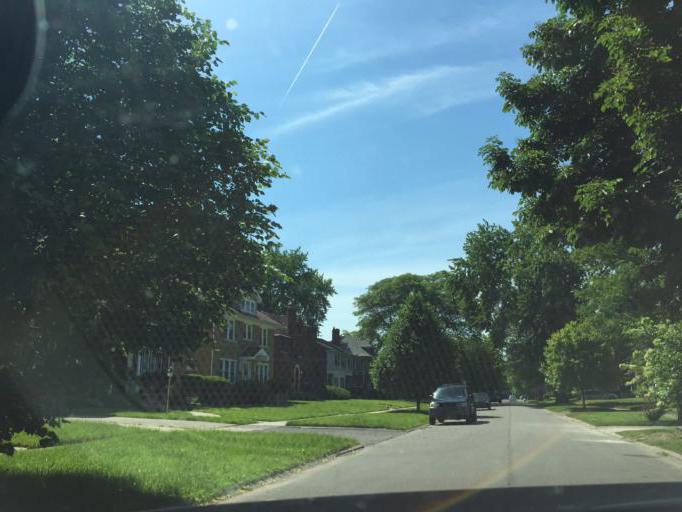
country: US
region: Michigan
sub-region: Oakland County
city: Southfield
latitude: 42.4064
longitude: -83.2298
